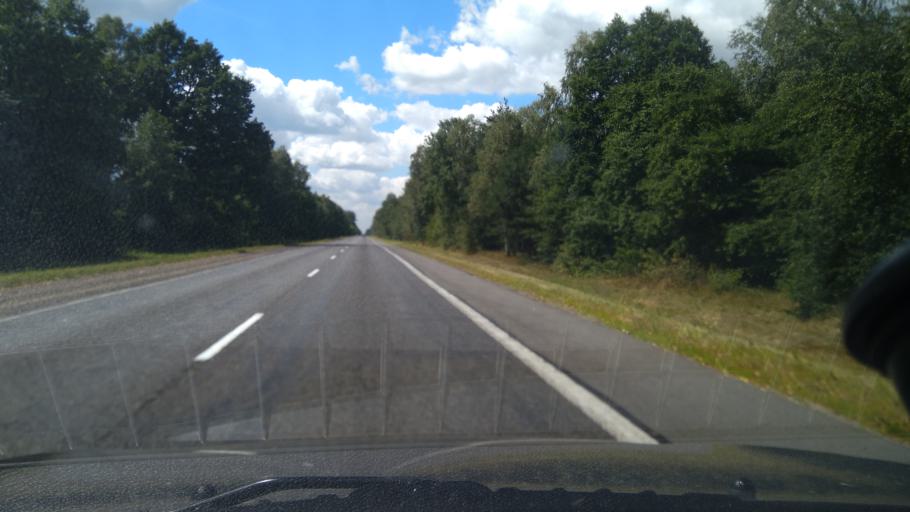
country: BY
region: Brest
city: Ivatsevichy
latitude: 52.6799
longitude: 25.2782
